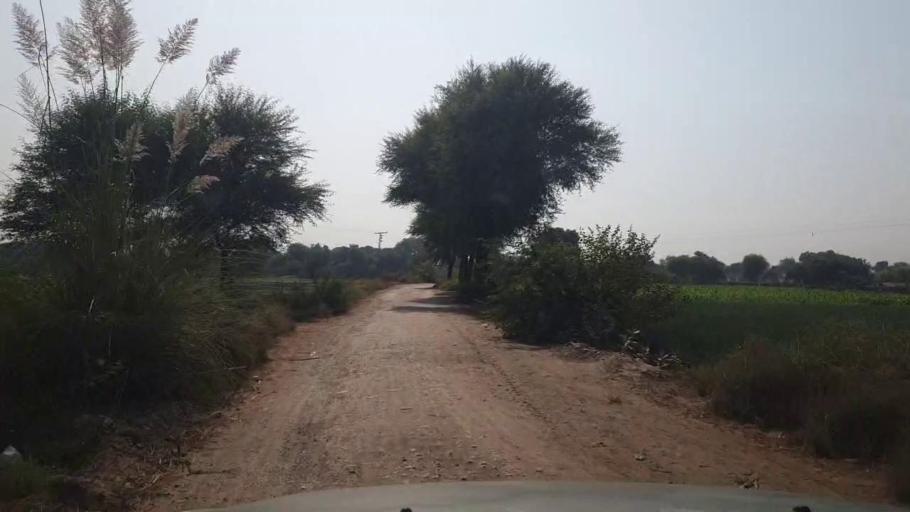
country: PK
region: Sindh
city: Bhit Shah
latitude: 25.7383
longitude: 68.5087
